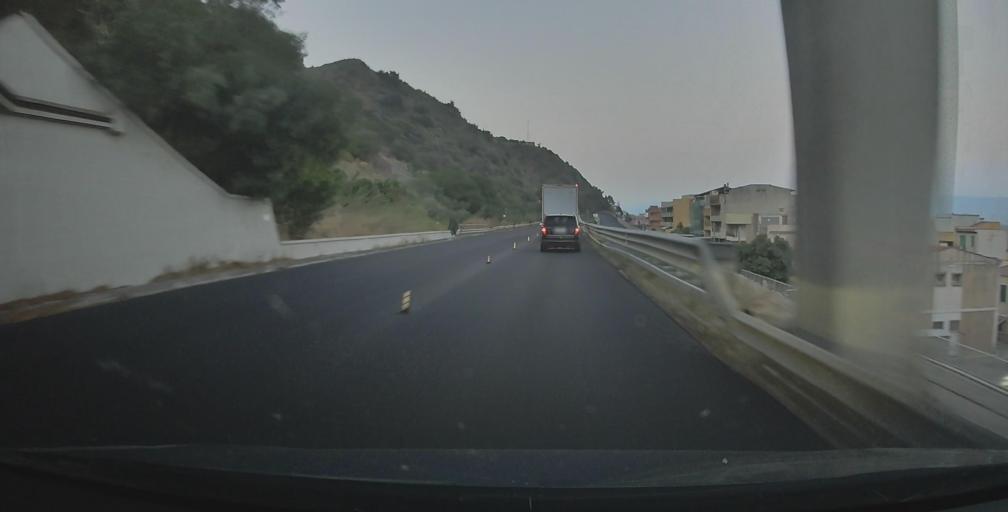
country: IT
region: Sicily
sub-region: Messina
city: Guidomandri Marina
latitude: 38.0437
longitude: 15.4596
